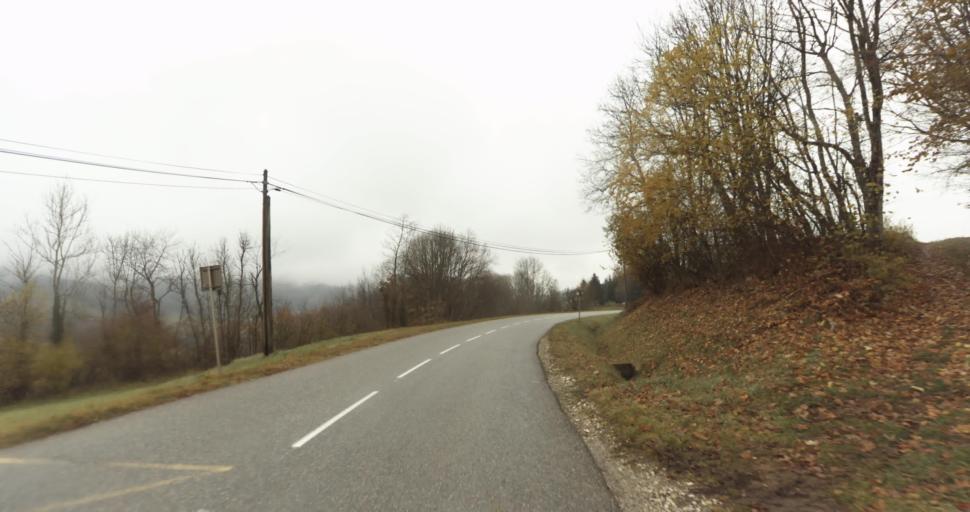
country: FR
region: Rhone-Alpes
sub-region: Departement de la Haute-Savoie
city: Etaux
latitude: 46.0246
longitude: 6.2873
